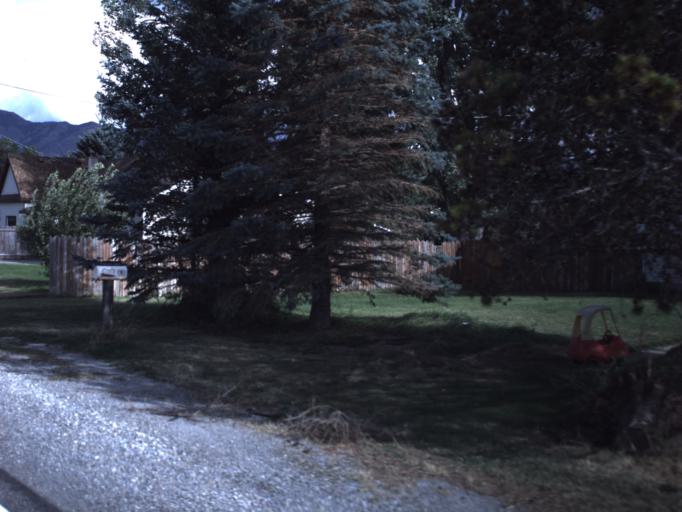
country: US
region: Utah
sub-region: Cache County
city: Lewiston
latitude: 41.9758
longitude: -111.8640
